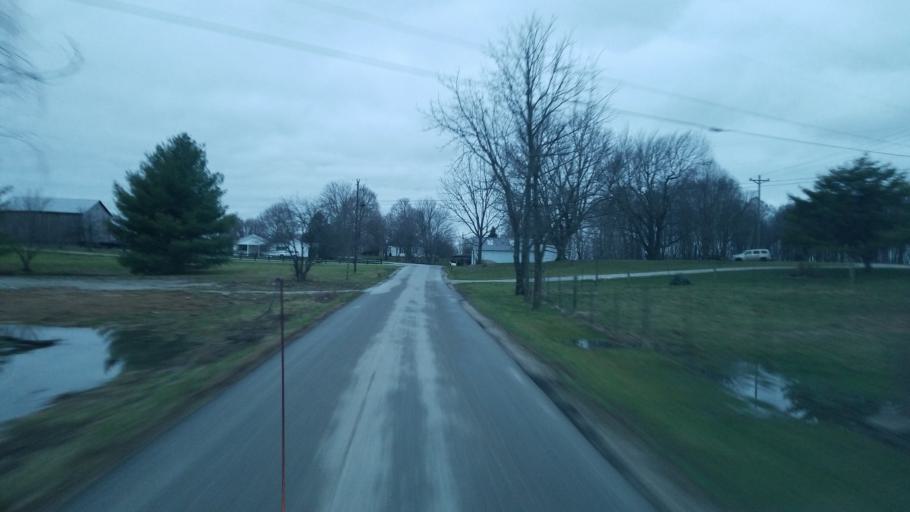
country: US
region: Kentucky
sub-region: Fleming County
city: Flemingsburg
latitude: 38.5035
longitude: -83.6738
